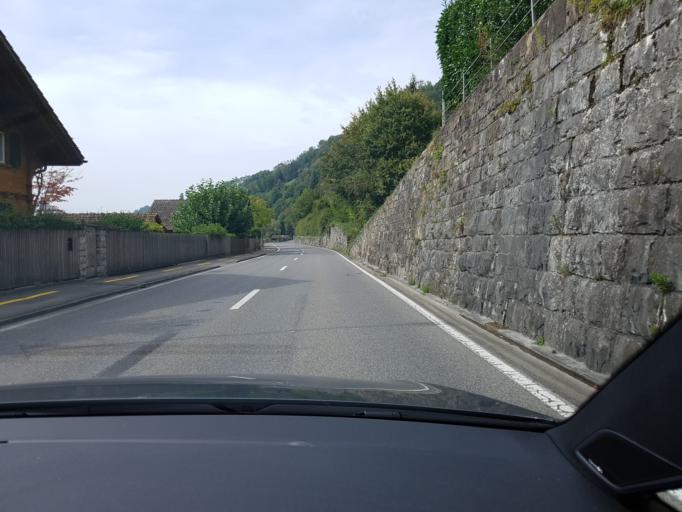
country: CH
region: Bern
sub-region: Thun District
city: Sigriswil
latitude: 46.7048
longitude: 7.7290
